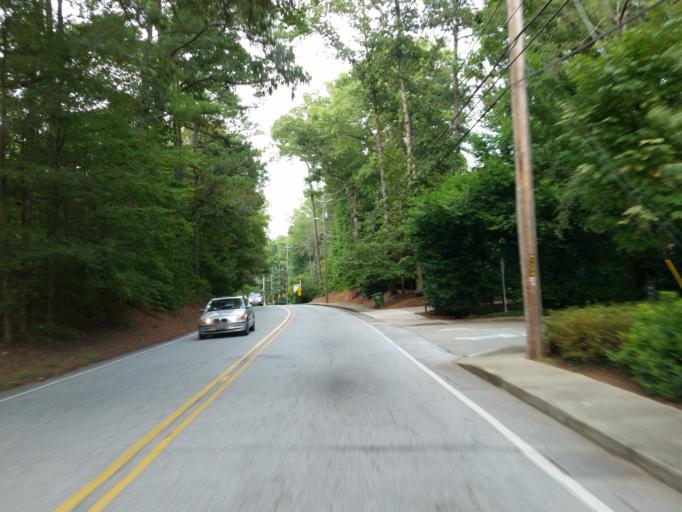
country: US
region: Georgia
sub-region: Cobb County
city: Vinings
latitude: 33.8385
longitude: -84.4182
